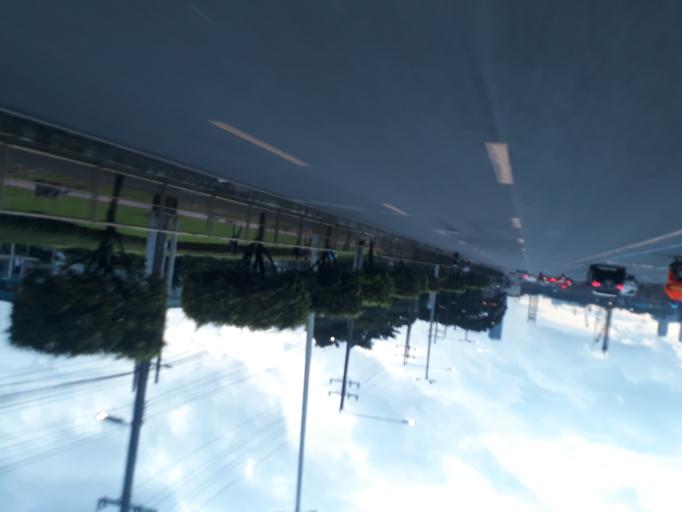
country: PH
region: Metro Manila
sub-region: Quezon City
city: Quezon City
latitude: 14.6567
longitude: 121.0571
